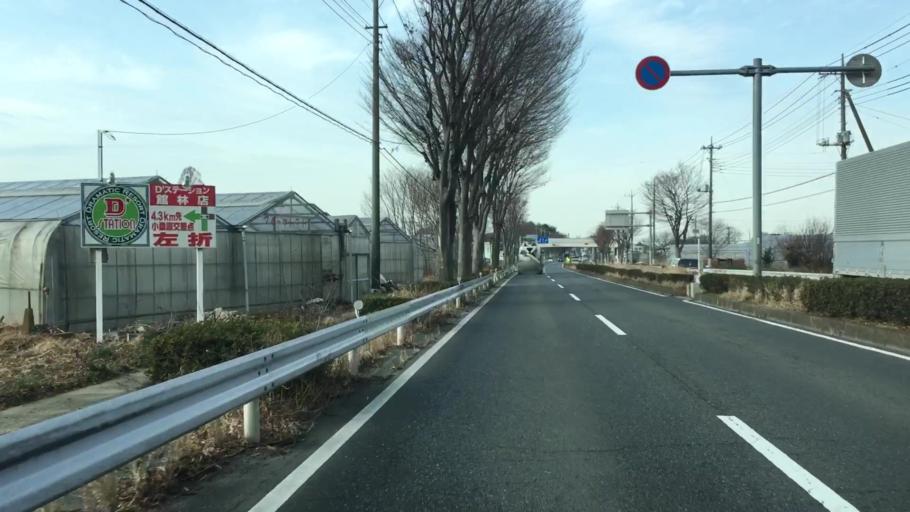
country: JP
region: Gunma
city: Tatebayashi
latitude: 36.2300
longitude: 139.5645
